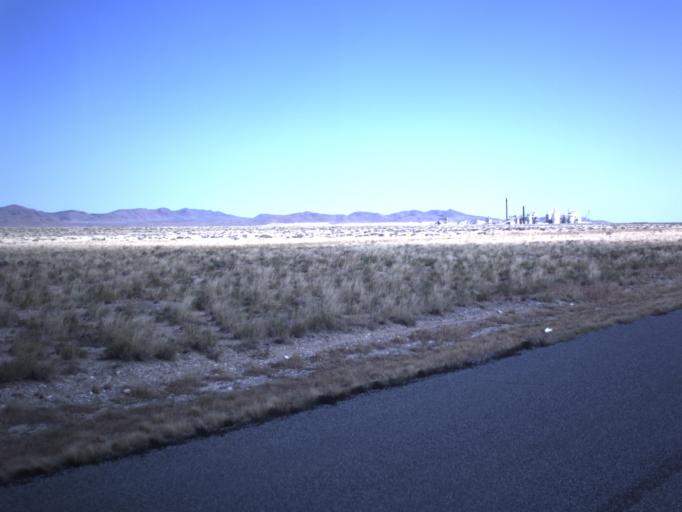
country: US
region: Utah
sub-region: Millard County
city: Fillmore
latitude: 38.9196
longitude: -112.8121
